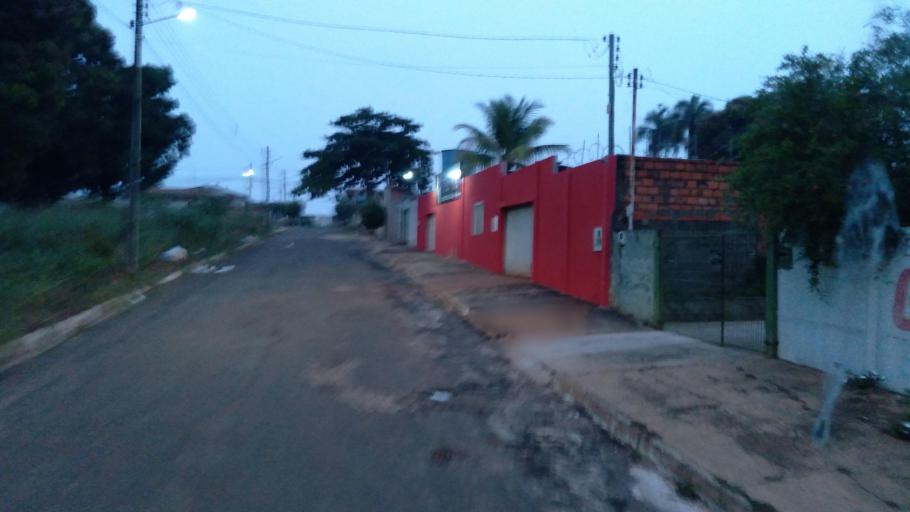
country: BR
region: Goias
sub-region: Mineiros
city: Mineiros
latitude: -17.5794
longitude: -52.5449
